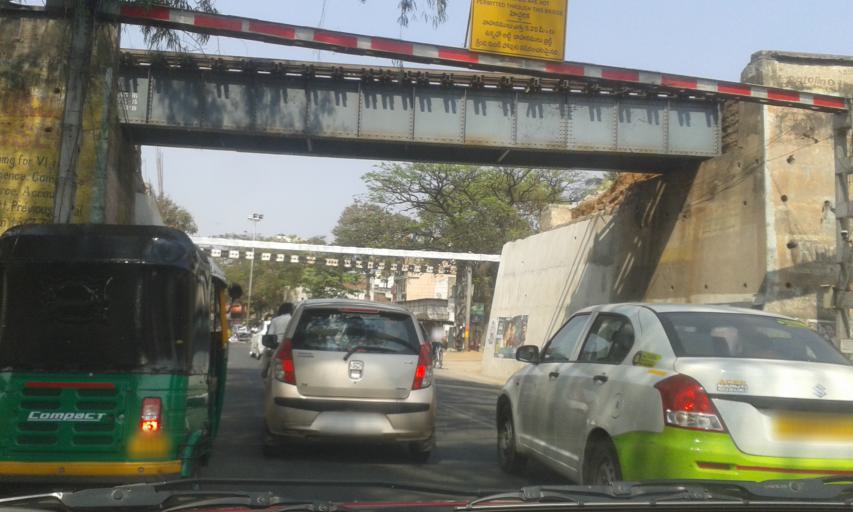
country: IN
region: Telangana
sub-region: Rangareddi
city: Secunderabad
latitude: 17.4912
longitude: 78.5127
